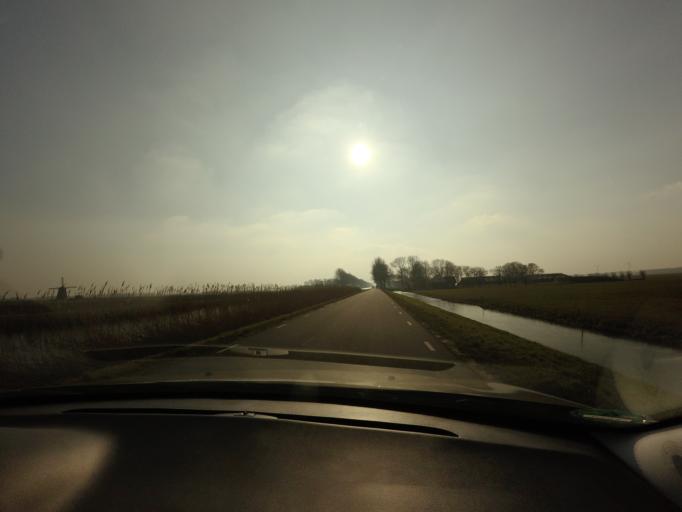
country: NL
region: North Holland
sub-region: Gemeente Alkmaar
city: Alkmaar
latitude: 52.6112
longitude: 4.7941
